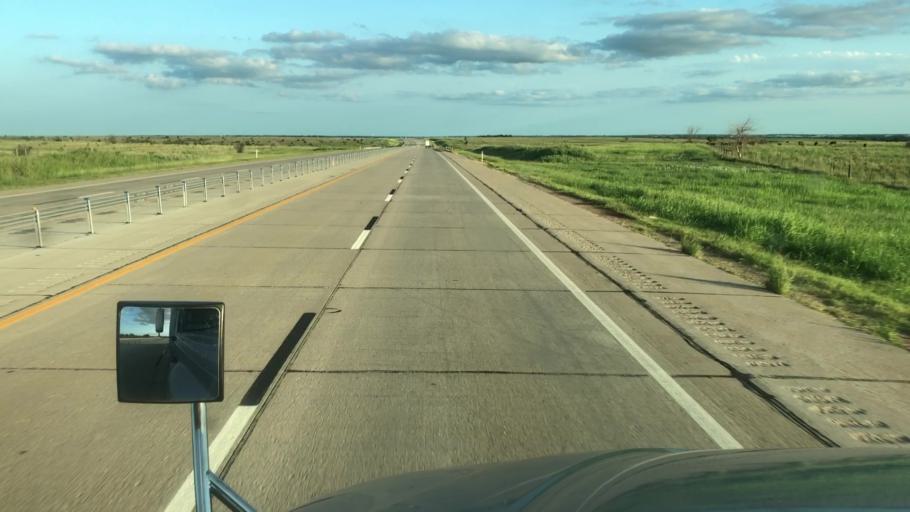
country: US
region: Oklahoma
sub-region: Pawnee County
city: Pawnee
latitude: 36.3574
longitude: -97.0319
